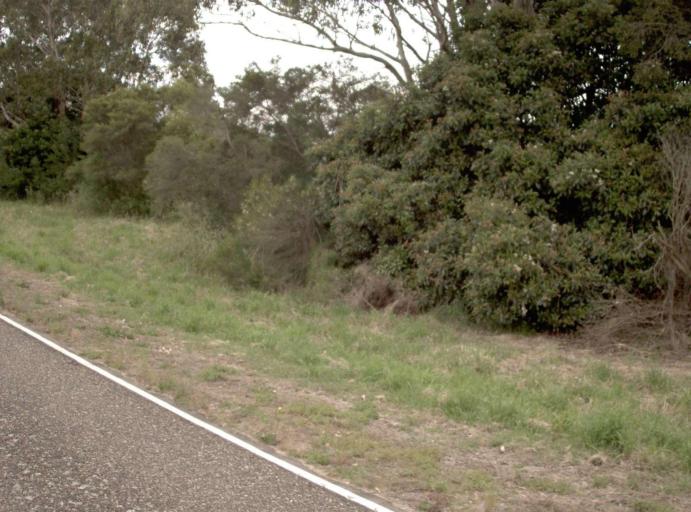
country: AU
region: Victoria
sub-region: East Gippsland
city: Bairnsdale
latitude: -37.7899
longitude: 147.3965
